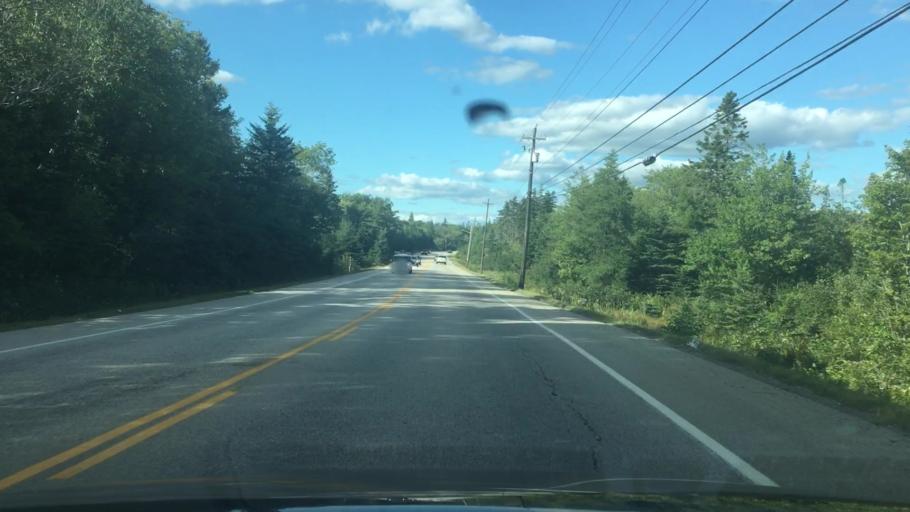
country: CA
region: Nova Scotia
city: Halifax
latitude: 44.6117
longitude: -63.6697
